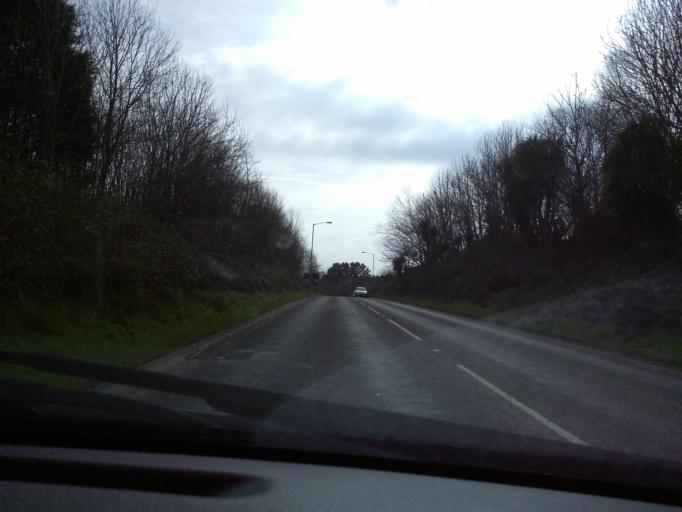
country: GB
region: England
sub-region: Cornwall
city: Penzance
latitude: 50.1273
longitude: -5.5475
